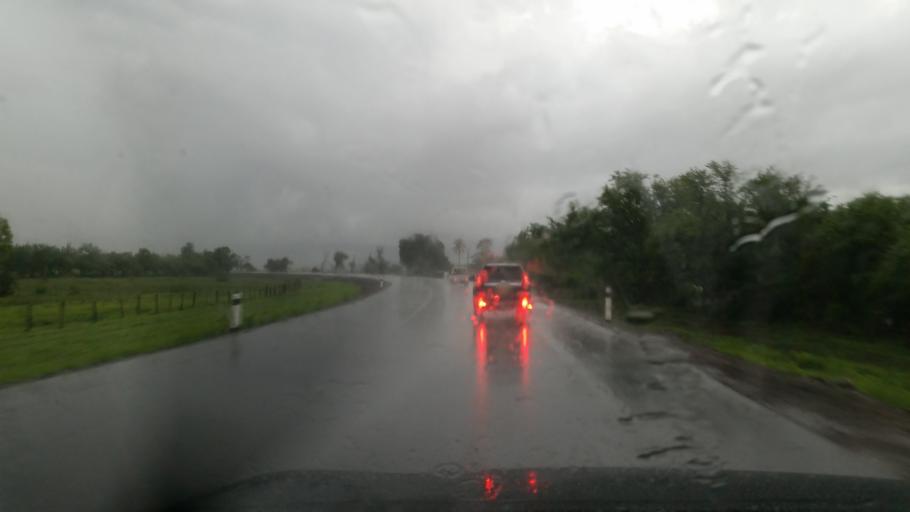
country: NI
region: Chinandega
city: Chichigalpa
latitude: 12.7846
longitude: -86.9368
